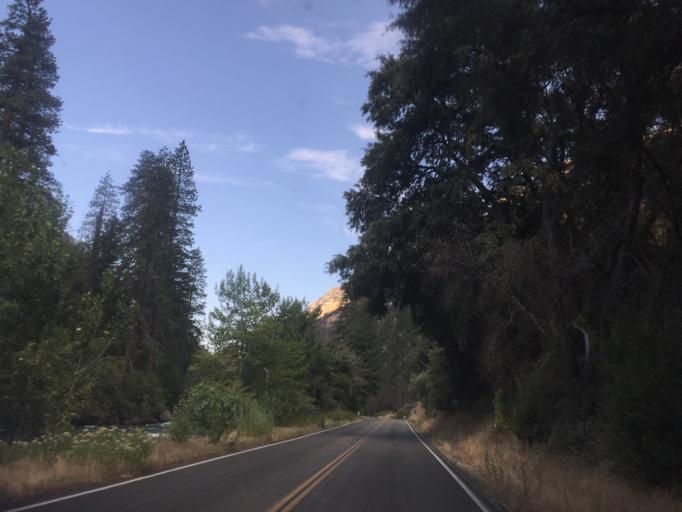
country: US
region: California
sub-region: Tulare County
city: Three Rivers
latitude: 36.8095
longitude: -118.7547
